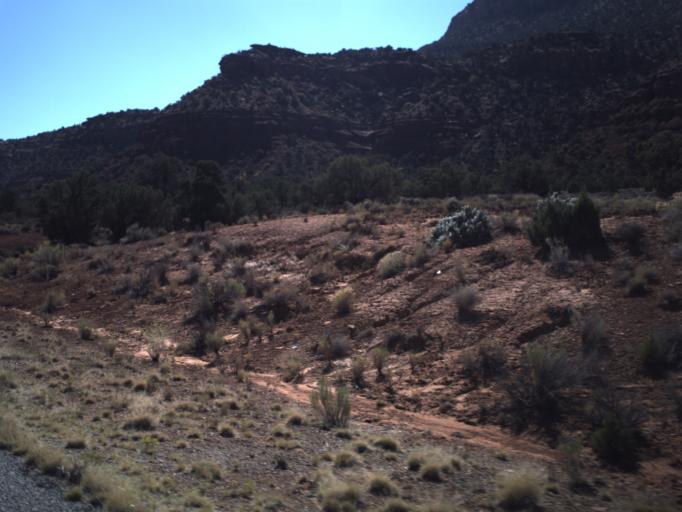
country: US
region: Utah
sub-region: San Juan County
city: Blanding
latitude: 37.6625
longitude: -110.1888
